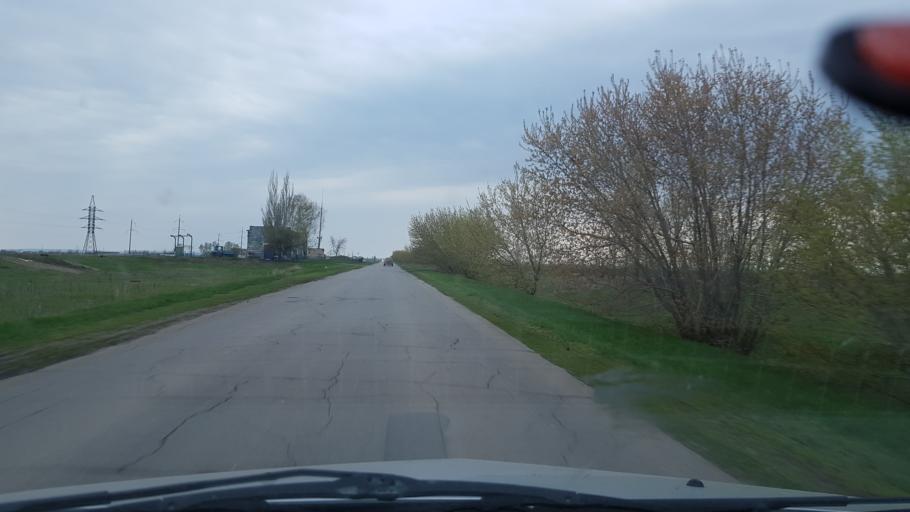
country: RU
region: Samara
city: Khryashchevka
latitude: 53.6705
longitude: 49.1116
